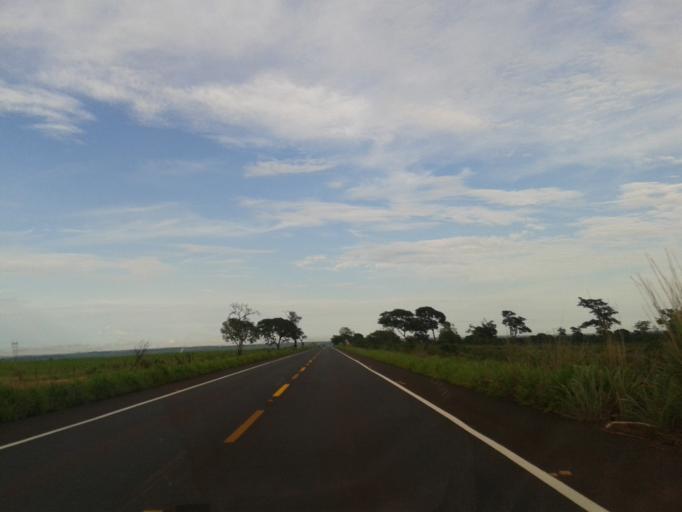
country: BR
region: Minas Gerais
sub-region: Santa Vitoria
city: Santa Vitoria
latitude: -19.0442
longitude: -50.4483
